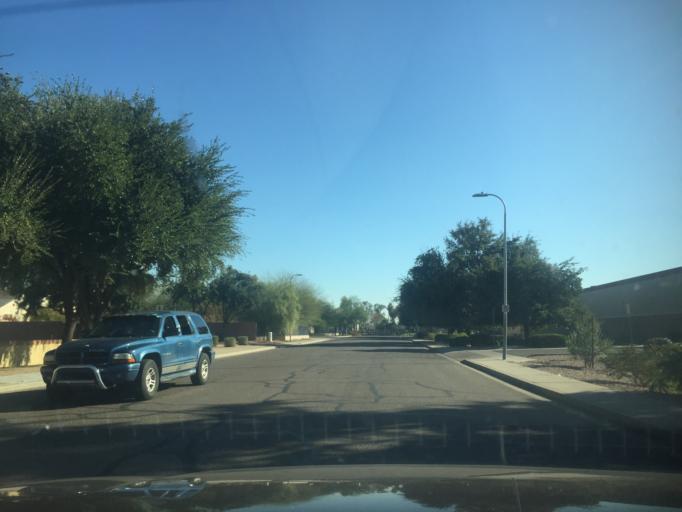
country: US
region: Arizona
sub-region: Maricopa County
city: Tolleson
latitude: 33.4765
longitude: -112.2190
